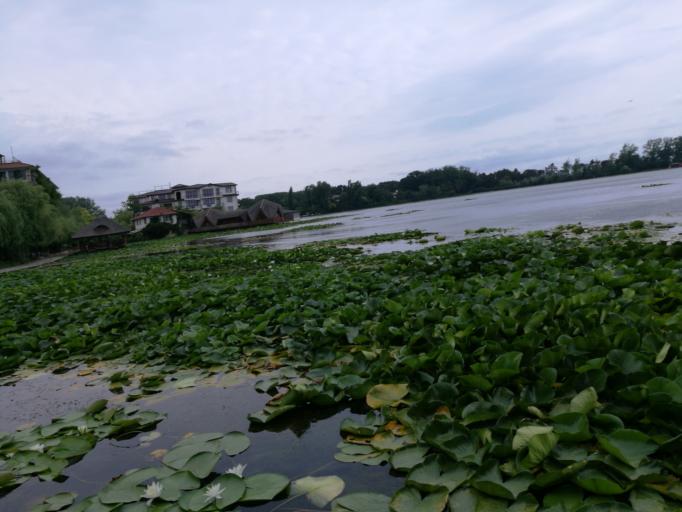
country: RO
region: Constanta
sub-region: Comuna Douazeci si Trei August
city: Douazeci si Trei August
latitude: 43.8672
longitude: 28.6003
